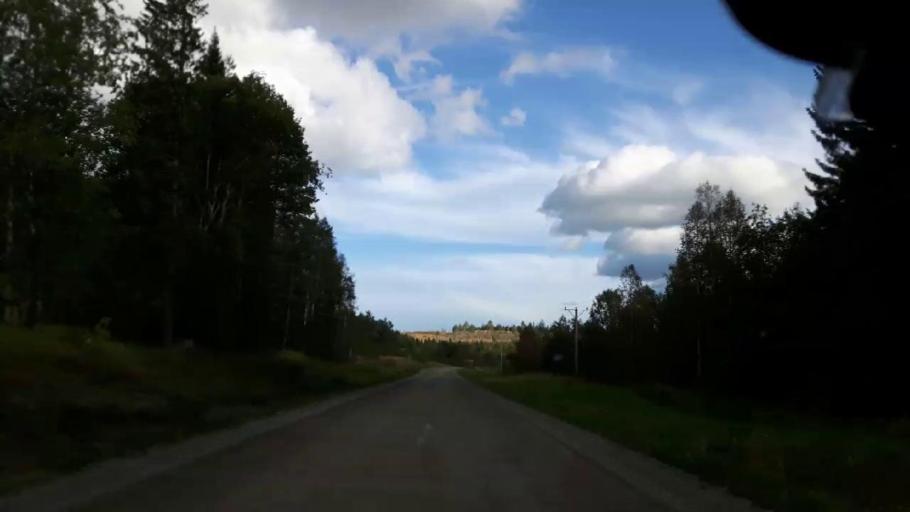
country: SE
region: Jaemtland
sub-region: Stroemsunds Kommun
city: Stroemsund
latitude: 63.3024
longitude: 15.5738
